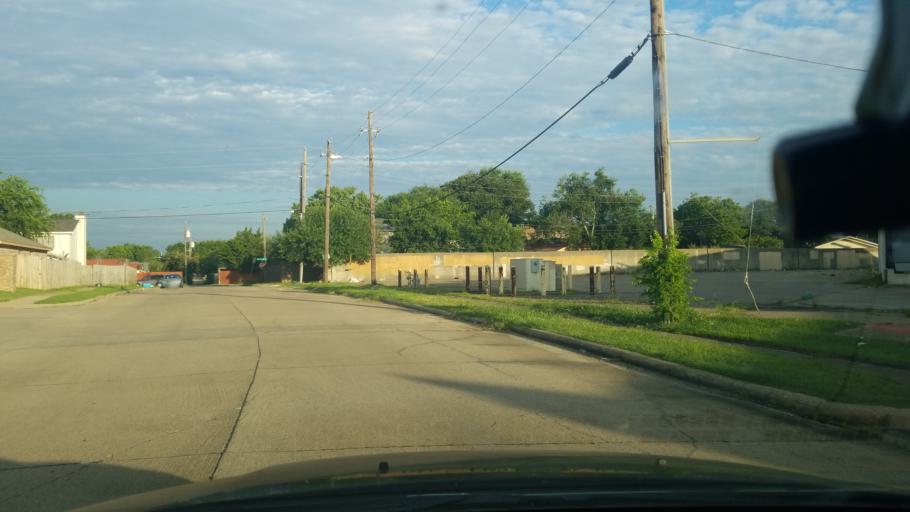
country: US
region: Texas
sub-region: Dallas County
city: Balch Springs
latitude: 32.7468
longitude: -96.6498
